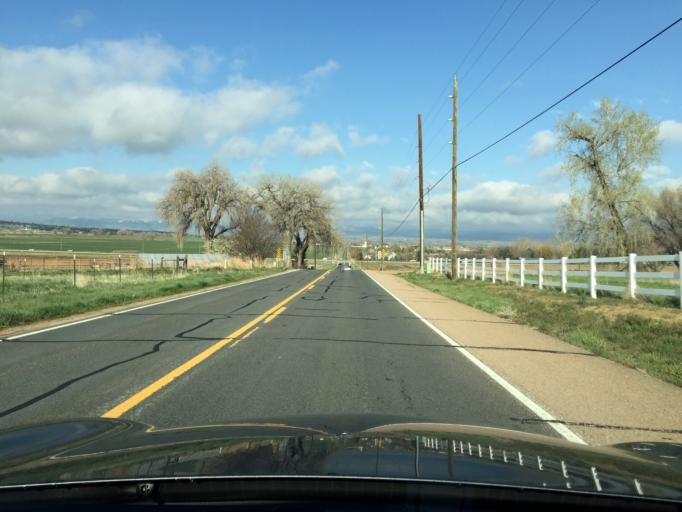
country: US
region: Colorado
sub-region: Boulder County
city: Longmont
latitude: 40.1163
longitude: -105.0970
